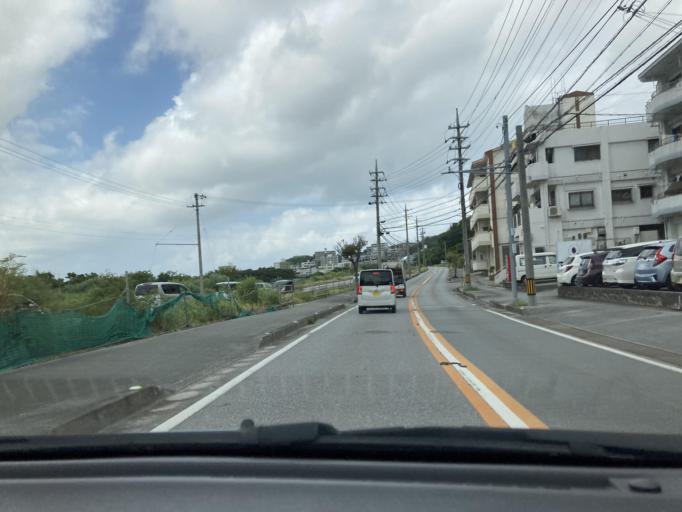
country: JP
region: Okinawa
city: Ginowan
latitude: 26.2394
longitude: 127.7575
